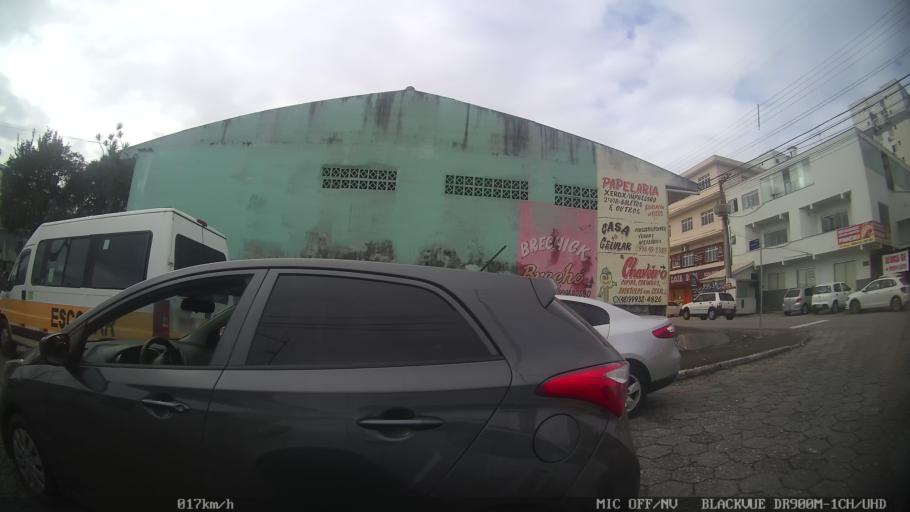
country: BR
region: Santa Catarina
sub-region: Sao Jose
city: Campinas
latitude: -27.5600
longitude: -48.6303
